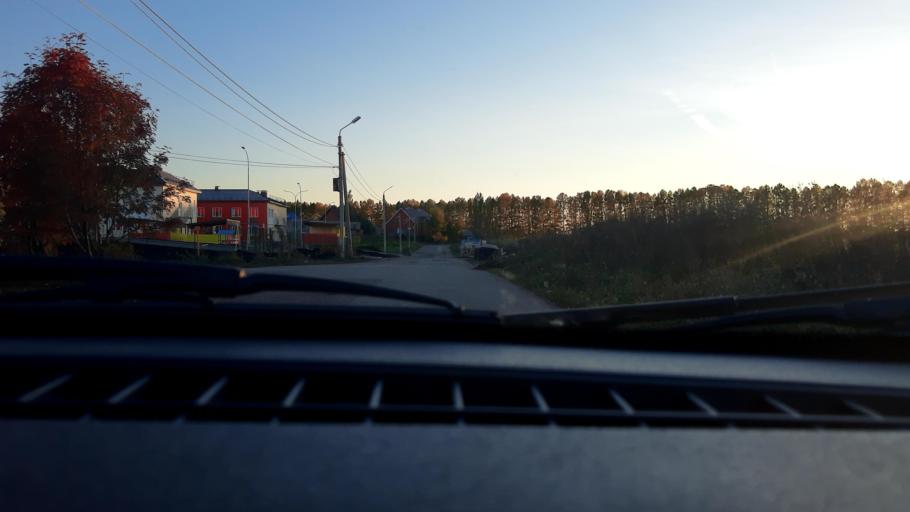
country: RU
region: Bashkortostan
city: Ufa
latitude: 54.8567
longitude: 56.0129
